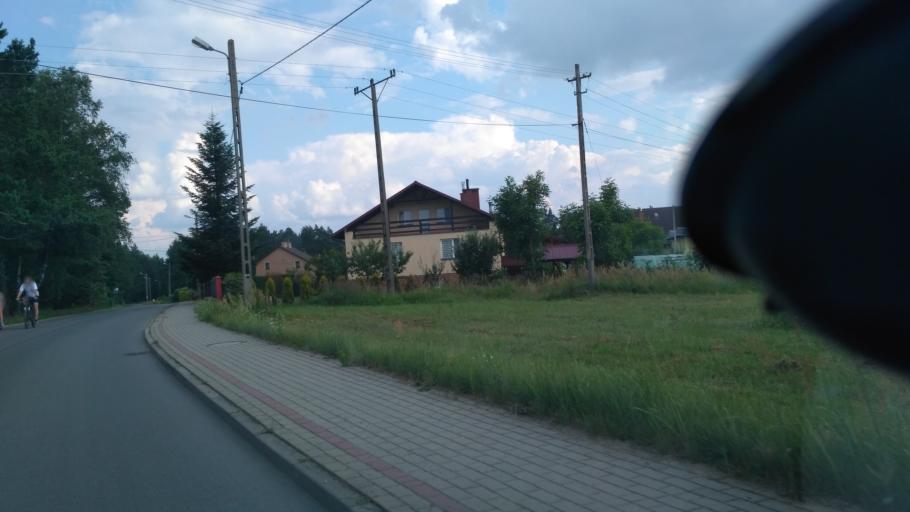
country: PL
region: Subcarpathian Voivodeship
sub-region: Powiat rzeszowski
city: Wysoka Glogowska
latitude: 50.1353
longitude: 22.0202
